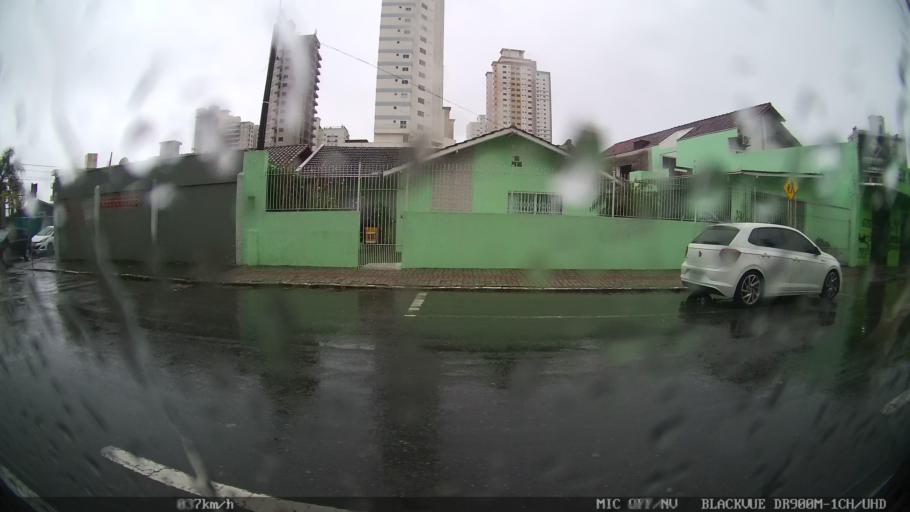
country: BR
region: Santa Catarina
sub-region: Itajai
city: Itajai
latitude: -26.9237
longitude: -48.6521
